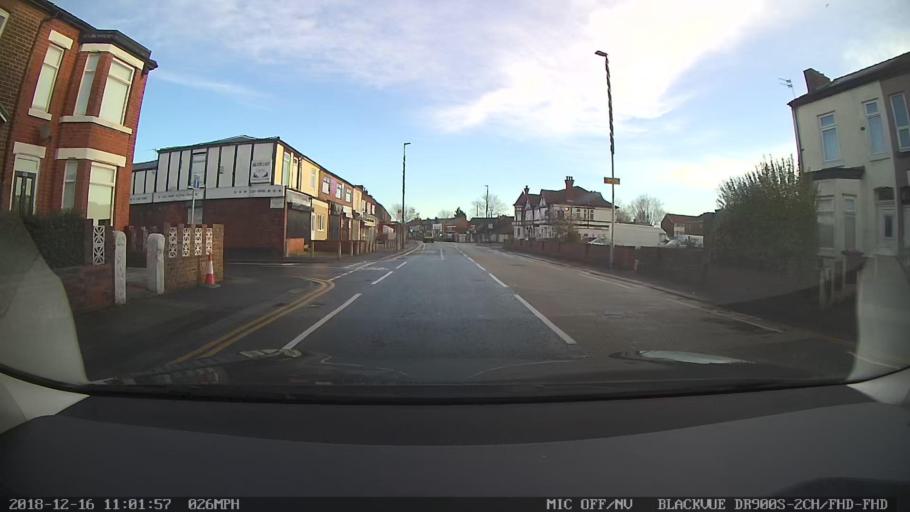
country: GB
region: England
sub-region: Manchester
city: Swinton
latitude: 53.4769
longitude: -2.3694
